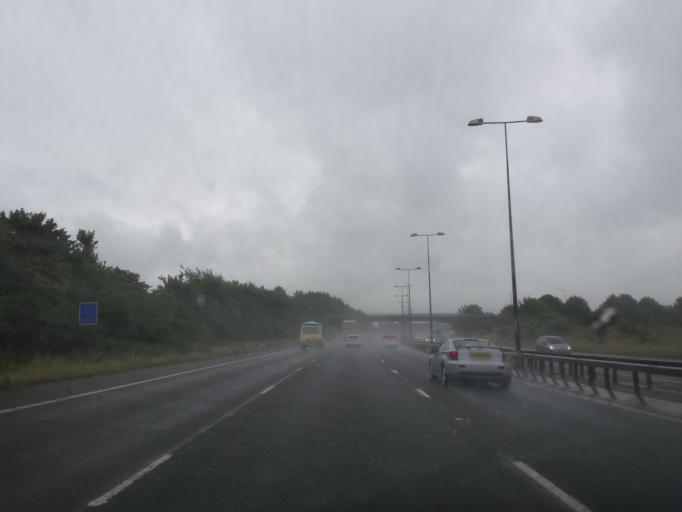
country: GB
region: England
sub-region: Derbyshire
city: Long Eaton
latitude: 52.9008
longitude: -1.2985
